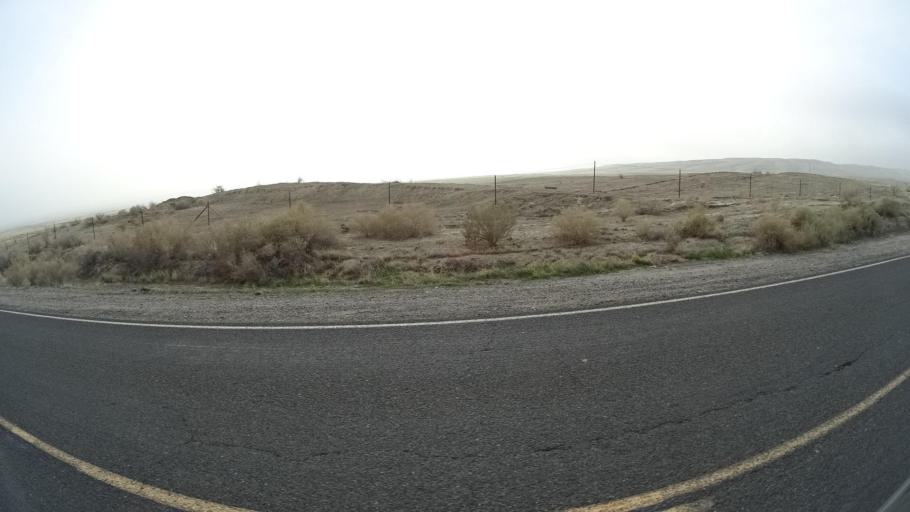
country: US
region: California
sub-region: Kern County
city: Ford City
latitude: 35.2413
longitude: -119.4527
